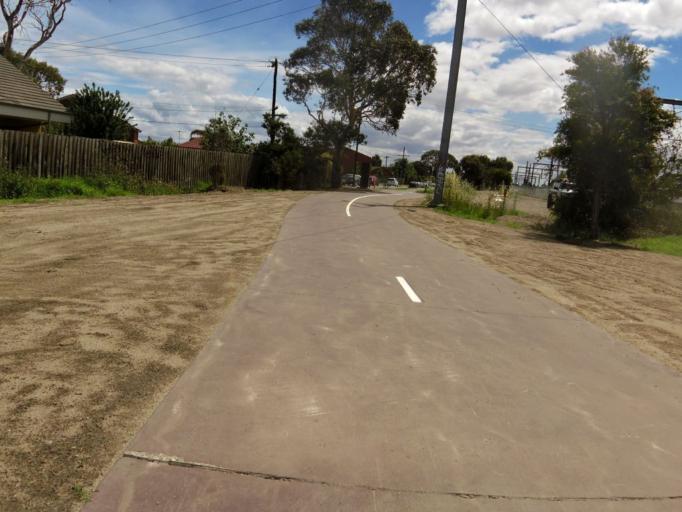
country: AU
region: Victoria
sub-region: Kingston
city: Clayton South
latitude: -37.9351
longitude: 145.1342
